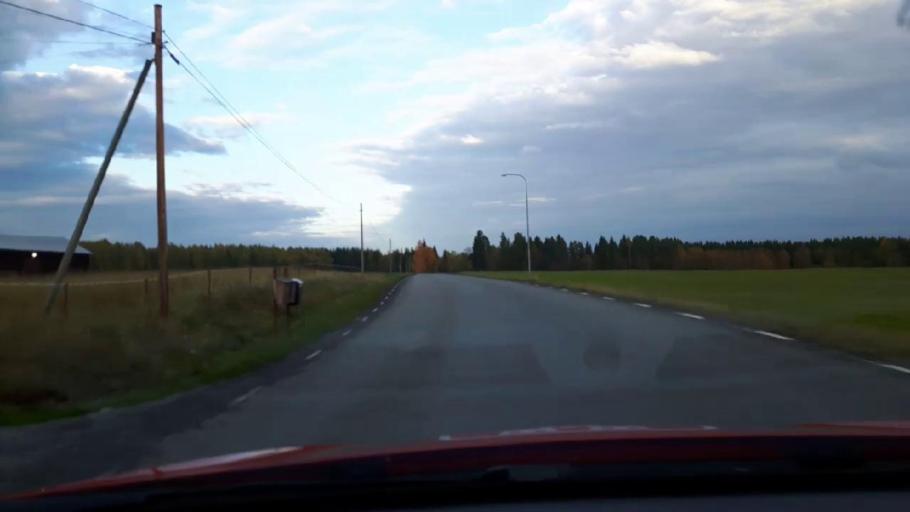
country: SE
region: Jaemtland
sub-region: OEstersunds Kommun
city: Lit
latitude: 63.3164
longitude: 14.9616
